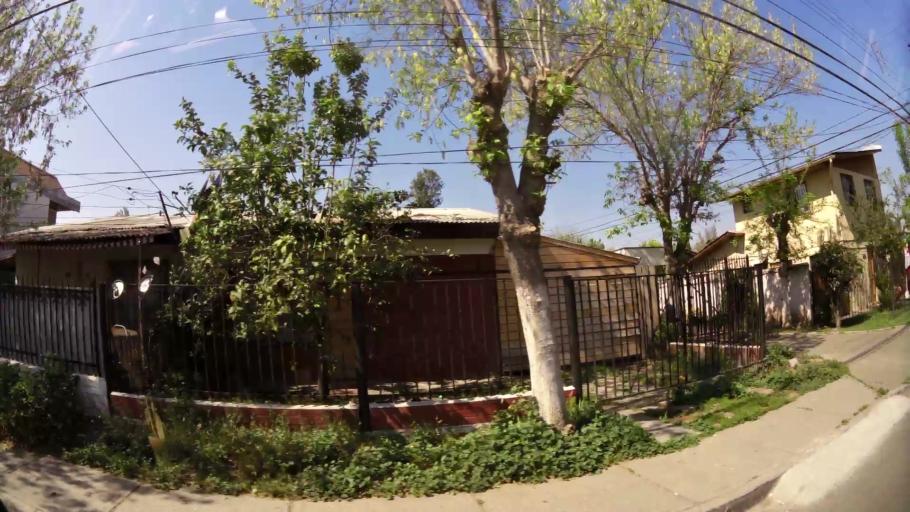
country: CL
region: Santiago Metropolitan
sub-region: Provincia de Talagante
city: Penaflor
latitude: -33.5726
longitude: -70.8182
